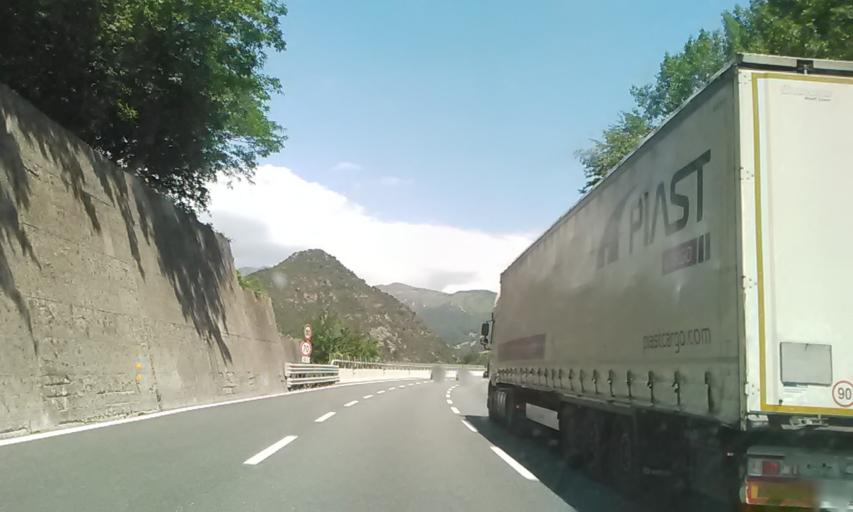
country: IT
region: Liguria
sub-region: Provincia di Genova
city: Mele
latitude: 44.4453
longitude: 8.7159
